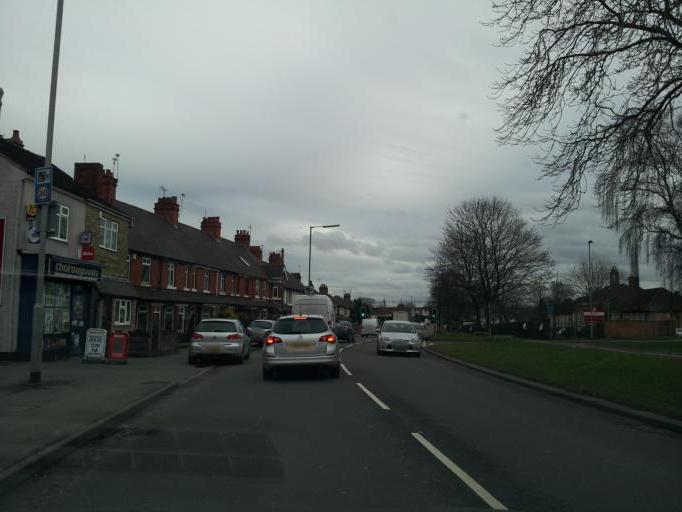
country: GB
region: England
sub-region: Staffordshire
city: Stafford
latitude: 52.7873
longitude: -2.1170
